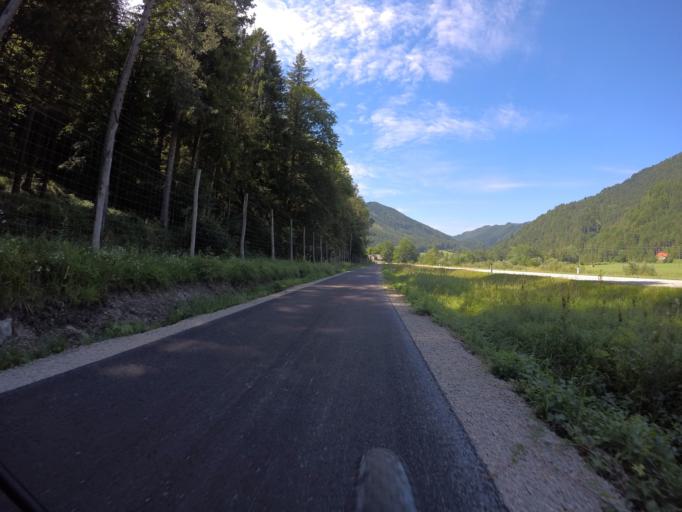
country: AT
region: Lower Austria
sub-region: Politischer Bezirk Amstetten
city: Hollenstein an der Ybbs
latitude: 47.8425
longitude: 14.7563
